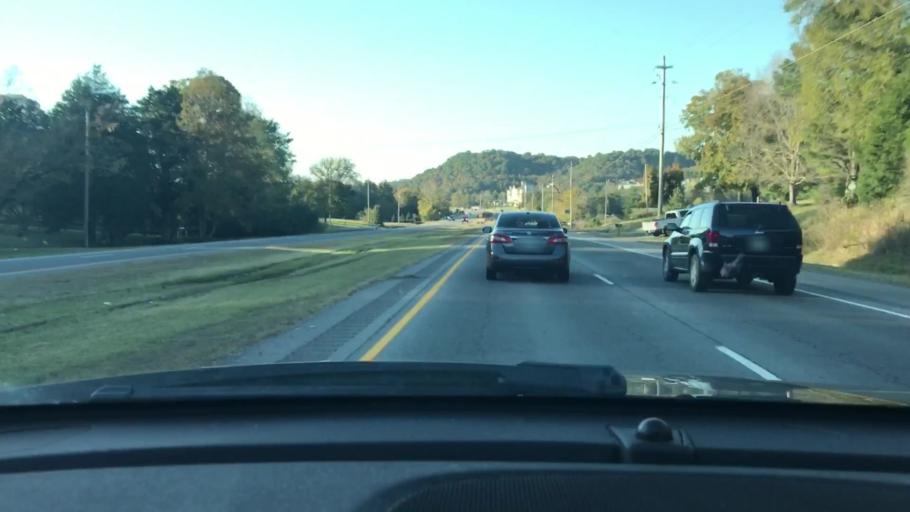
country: US
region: Tennessee
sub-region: Cheatham County
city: Ashland City
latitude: 36.2385
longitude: -87.0214
